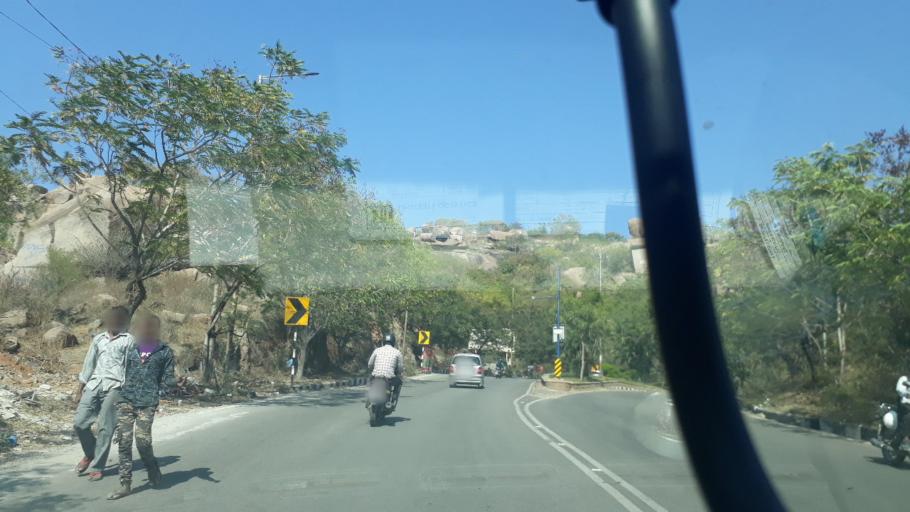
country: IN
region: Telangana
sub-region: Rangareddi
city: Kukatpalli
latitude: 17.4176
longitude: 78.3950
